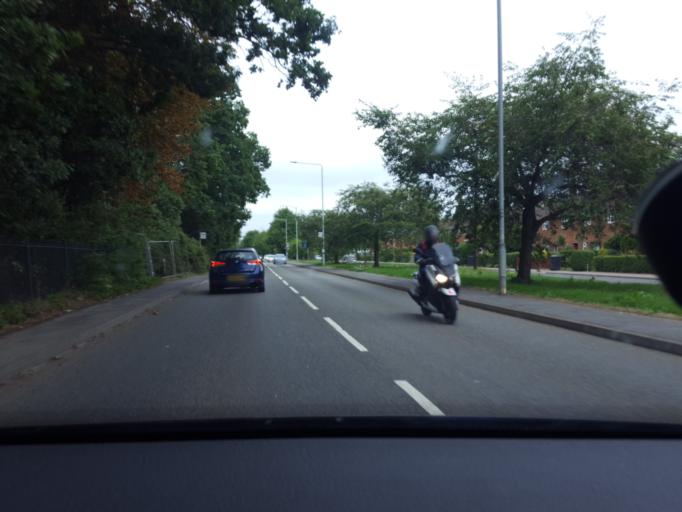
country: GB
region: England
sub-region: Leicestershire
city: Loughborough
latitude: 52.7687
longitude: -1.2335
